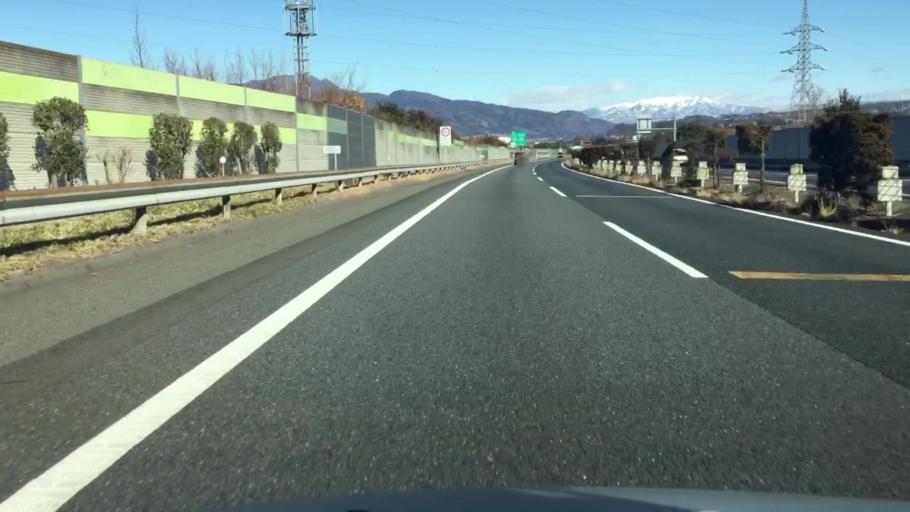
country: JP
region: Gunma
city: Shibukawa
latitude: 36.4671
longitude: 139.0117
